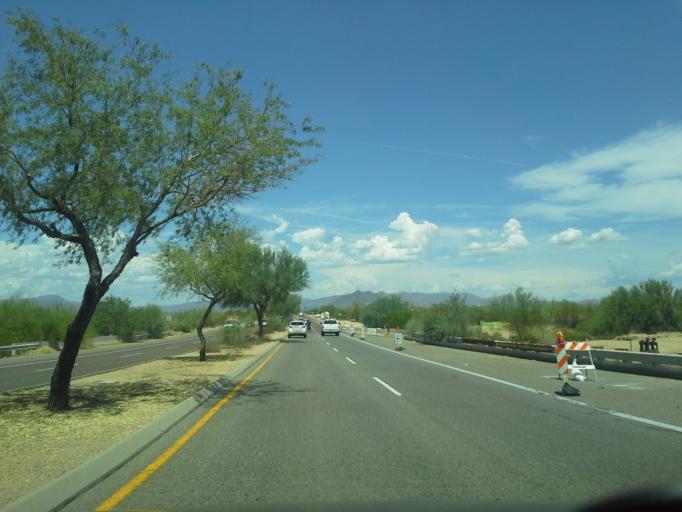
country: US
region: Arizona
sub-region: Maricopa County
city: Cave Creek
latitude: 33.7231
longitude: -112.0106
